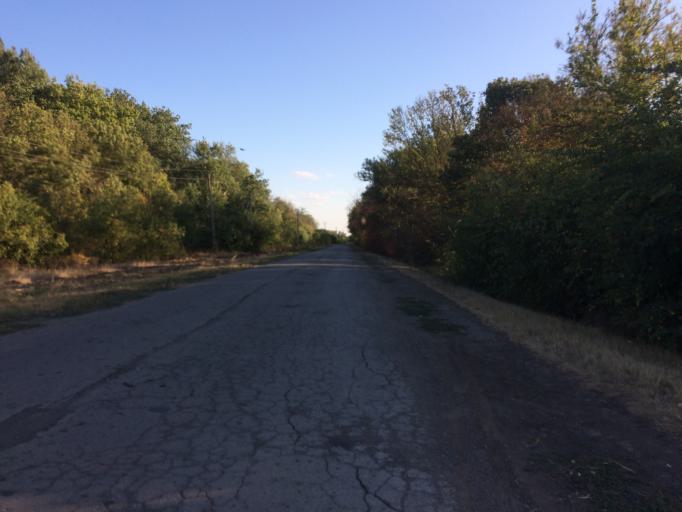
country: RU
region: Rostov
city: Gigant
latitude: 46.5131
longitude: 41.1921
